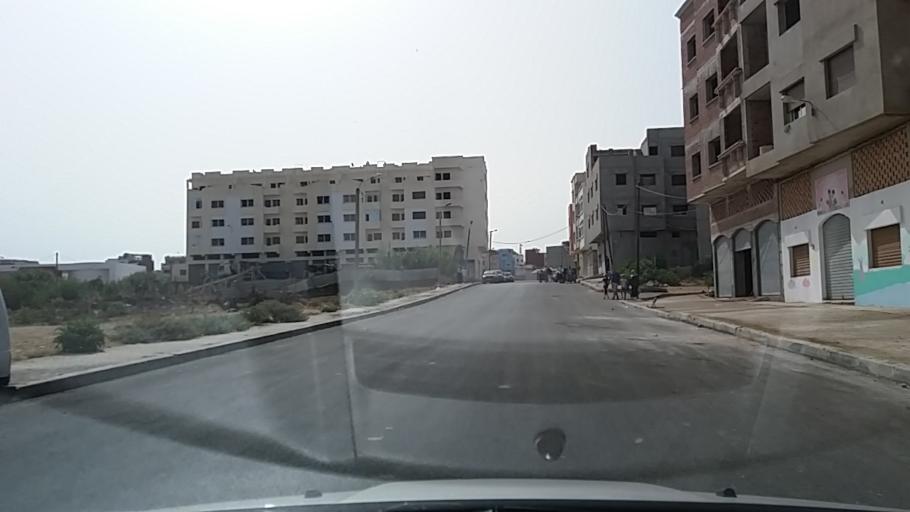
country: MA
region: Tanger-Tetouan
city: Asilah
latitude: 35.4614
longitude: -6.0411
